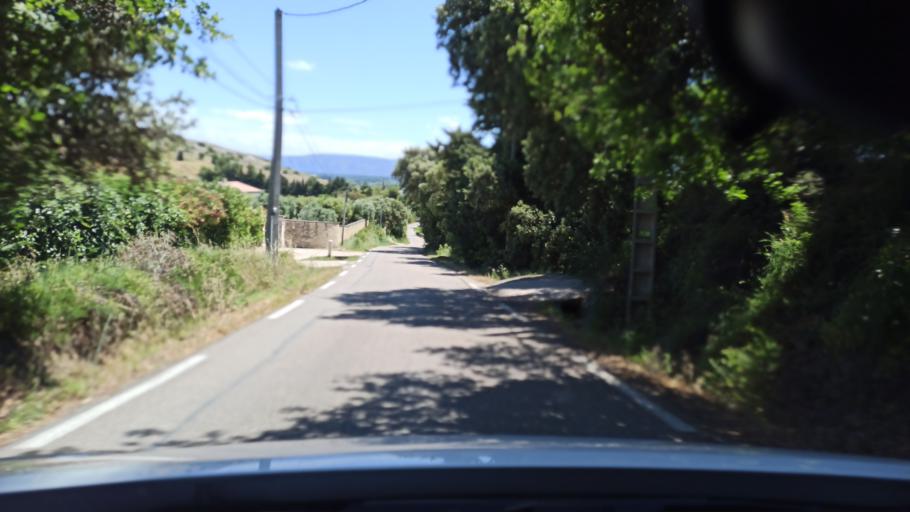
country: FR
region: Provence-Alpes-Cote d'Azur
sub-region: Departement du Vaucluse
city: Caumont-sur-Durance
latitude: 43.8991
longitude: 4.9354
